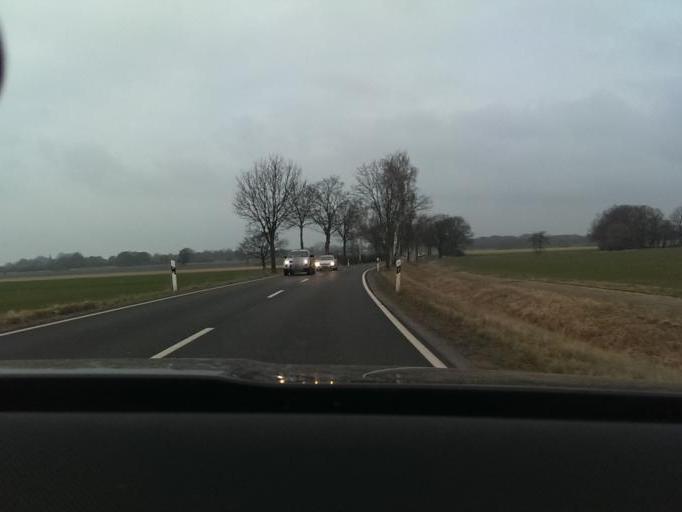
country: DE
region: Lower Saxony
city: Isernhagen Farster Bauerschaft
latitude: 52.4482
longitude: 9.8384
